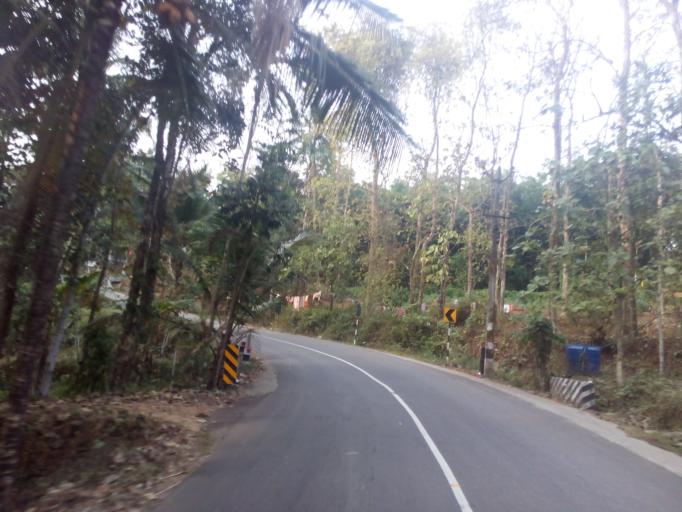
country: IN
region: Kerala
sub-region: Kottayam
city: Palackattumala
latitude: 9.8145
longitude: 76.6679
